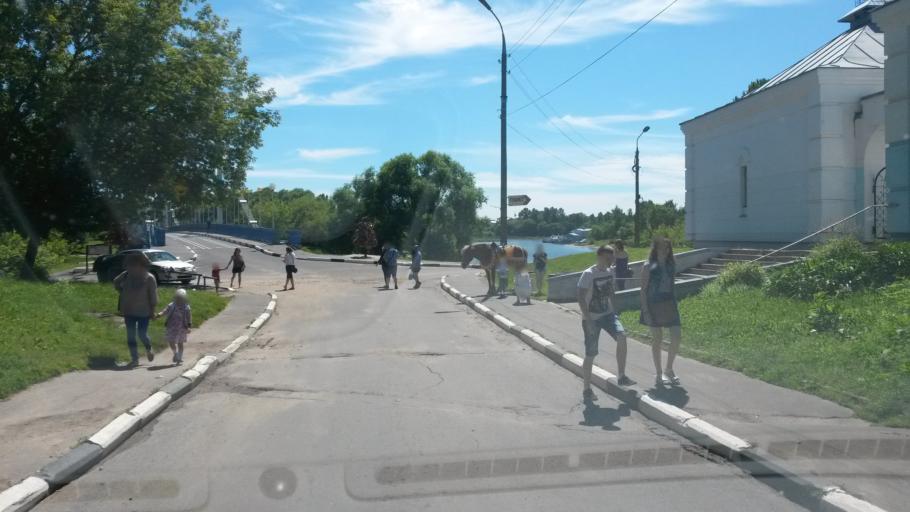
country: RU
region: Jaroslavl
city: Yaroslavl
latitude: 57.6216
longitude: 39.8971
